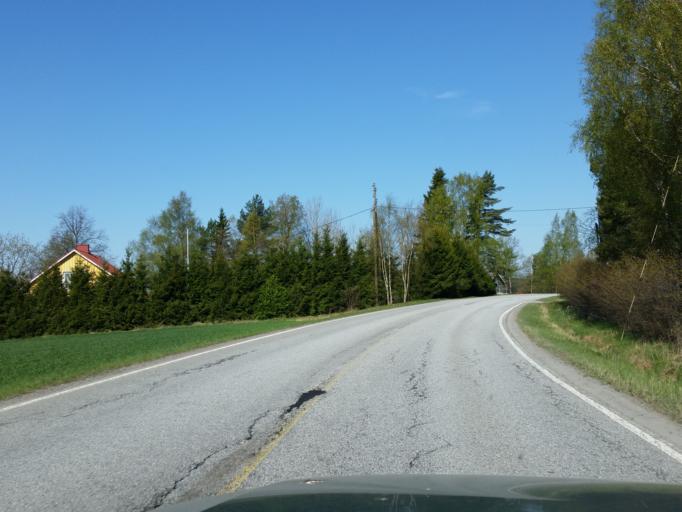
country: FI
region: Uusimaa
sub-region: Helsinki
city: Lohja
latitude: 60.1732
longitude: 24.0964
